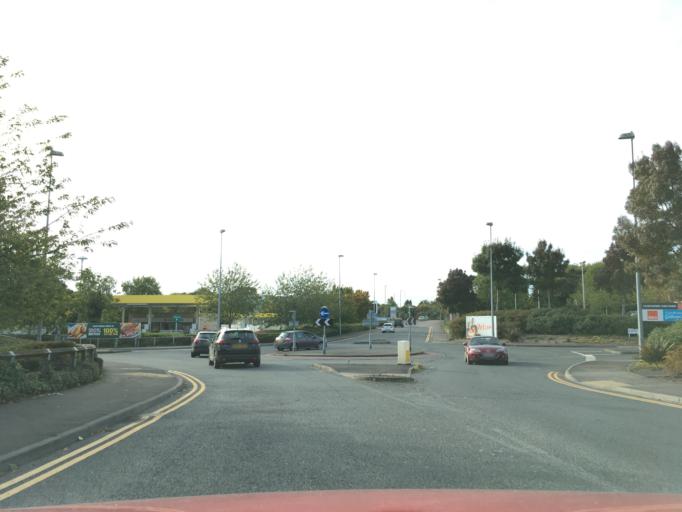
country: GB
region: England
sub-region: South Gloucestershire
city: Almondsbury
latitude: 51.5274
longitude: -2.6037
